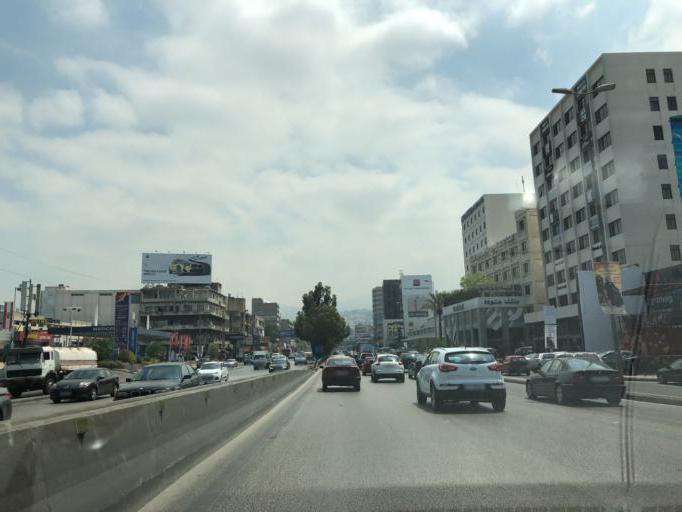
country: LB
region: Mont-Liban
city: Jdaidet el Matn
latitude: 33.8941
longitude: 35.5535
